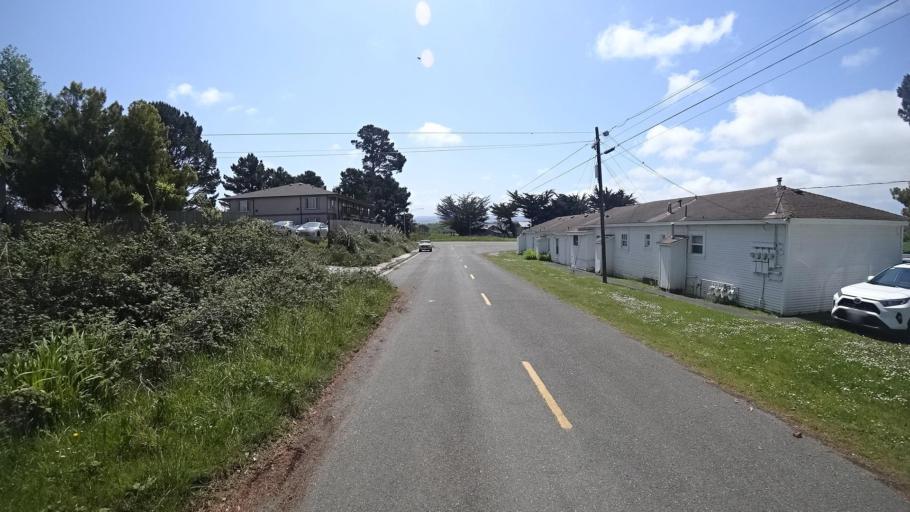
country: US
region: California
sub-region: Humboldt County
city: Ferndale
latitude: 40.6390
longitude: -124.2254
